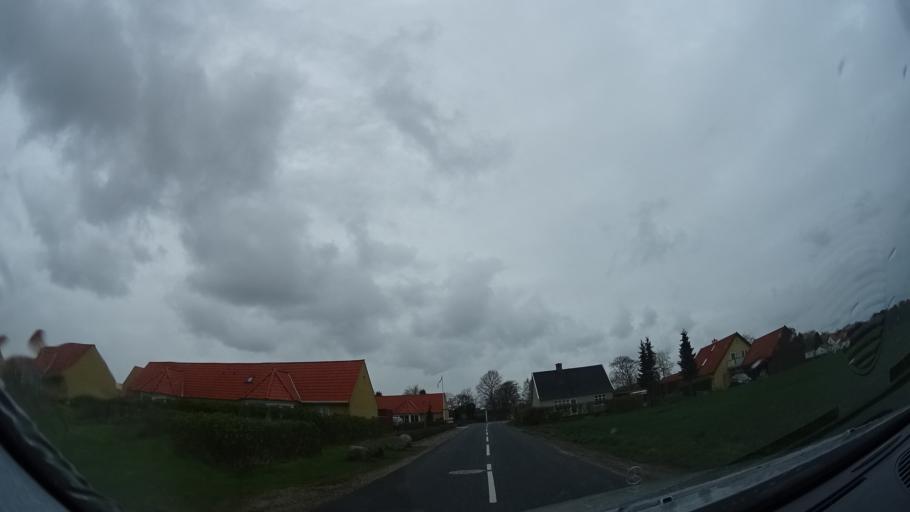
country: DK
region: Zealand
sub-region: Holbaek Kommune
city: Vipperod
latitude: 55.7029
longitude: 11.7773
